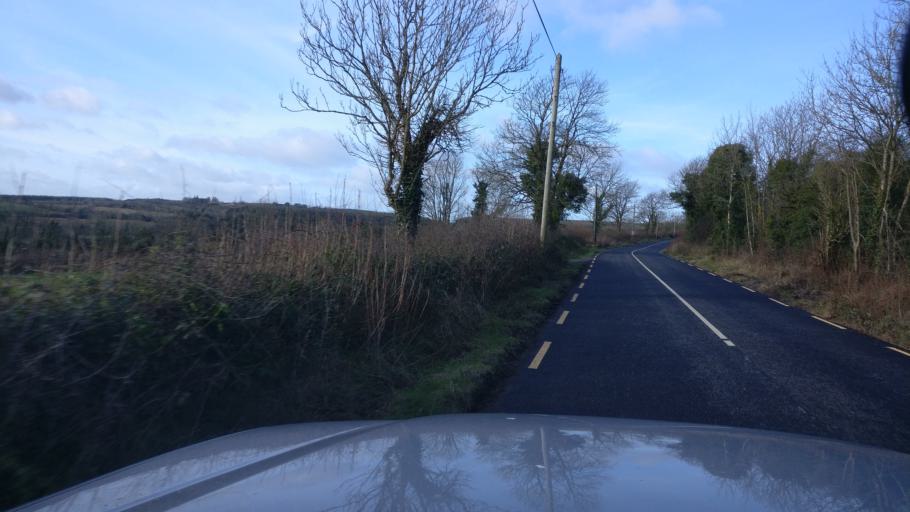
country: IE
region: Leinster
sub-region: Kilkenny
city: Castlecomer
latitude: 52.8978
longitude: -7.1735
